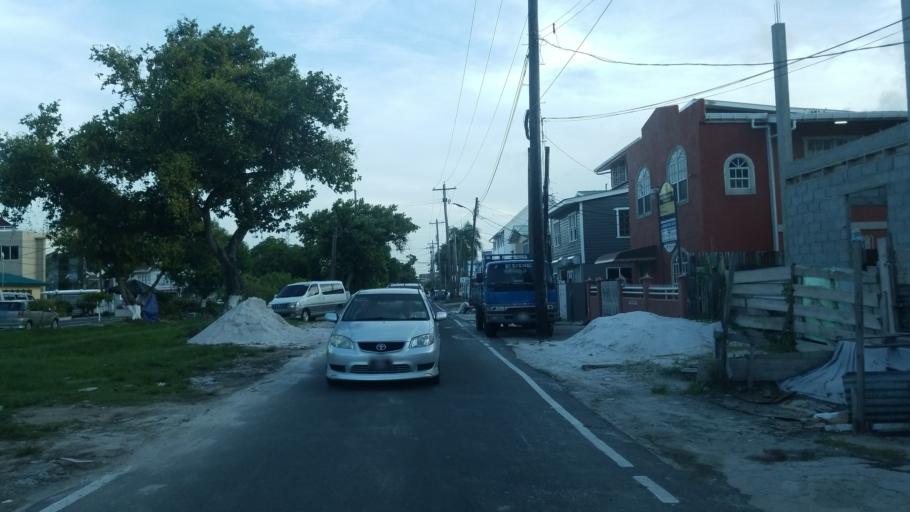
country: GY
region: Demerara-Mahaica
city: Georgetown
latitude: 6.8189
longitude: -58.1603
